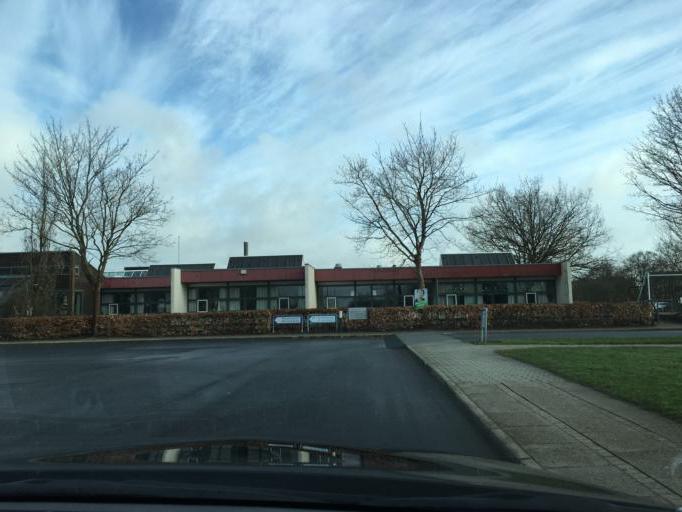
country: DK
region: South Denmark
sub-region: Kolding Kommune
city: Kolding
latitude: 55.5014
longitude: 9.4490
